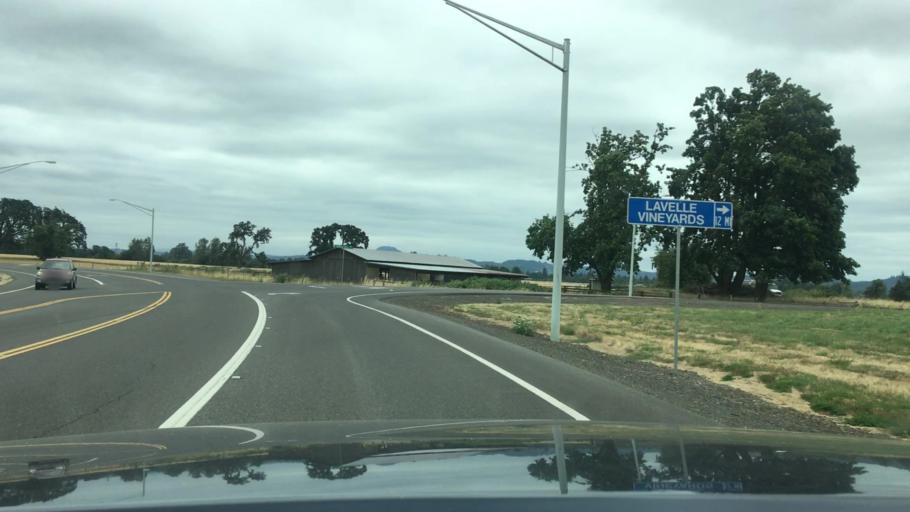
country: US
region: Oregon
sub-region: Lane County
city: Junction City
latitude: 44.1116
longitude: -123.2079
